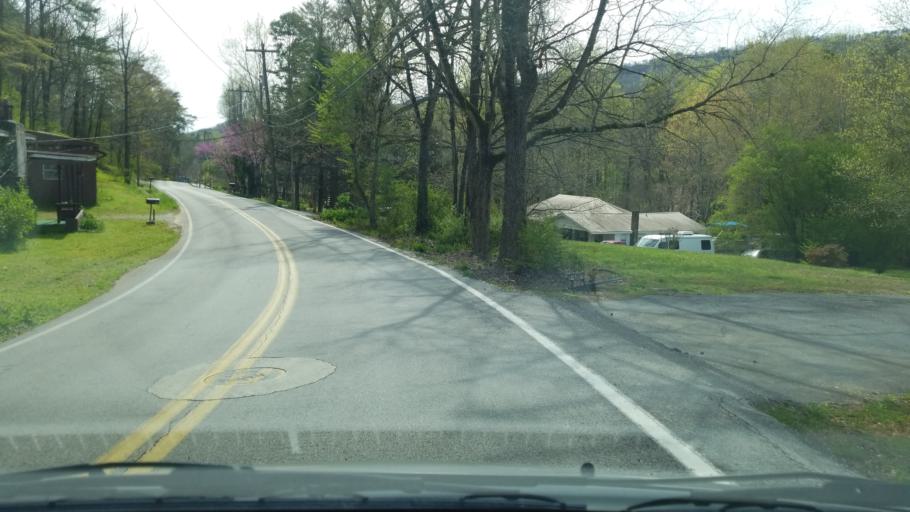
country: US
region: Tennessee
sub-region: Hamilton County
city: Walden
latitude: 35.1676
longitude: -85.2728
